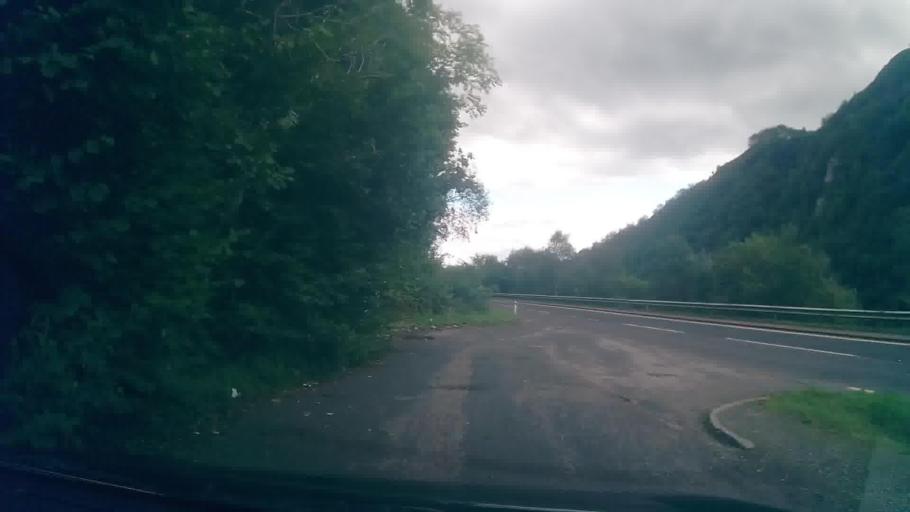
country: GB
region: Scotland
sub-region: Argyll and Bute
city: Oban
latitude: 56.3966
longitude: -5.1282
